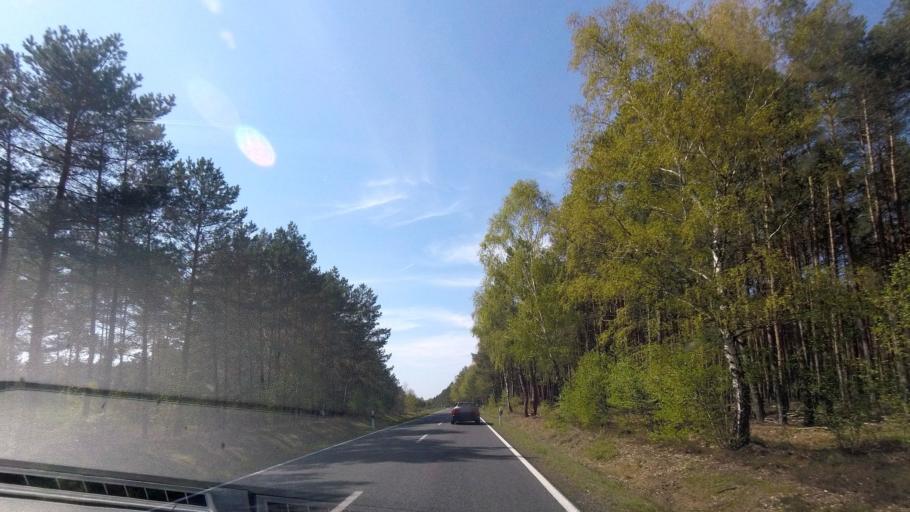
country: DE
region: Brandenburg
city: Gorzke
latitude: 52.1706
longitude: 12.4250
